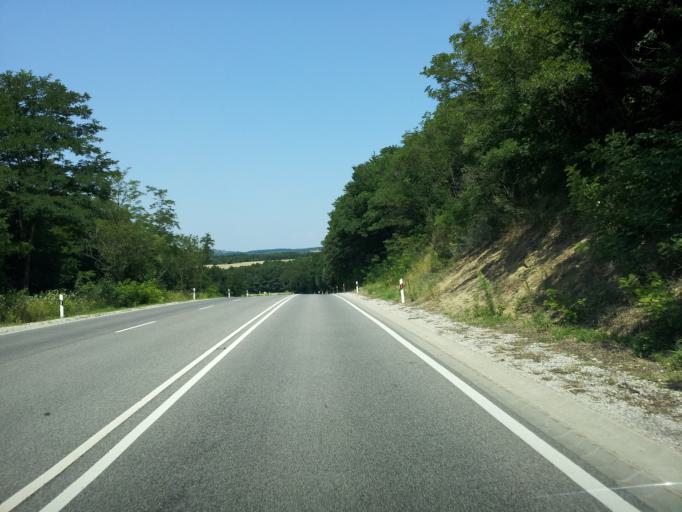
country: HU
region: Zala
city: Zalaegerszeg
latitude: 46.8274
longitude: 16.9557
